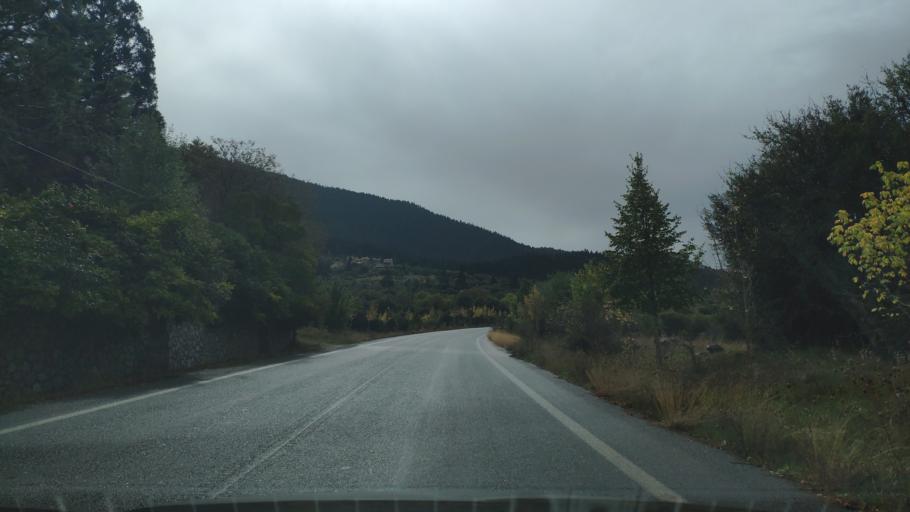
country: GR
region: Peloponnese
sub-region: Nomos Arkadias
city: Langadhia
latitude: 37.6703
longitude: 22.1941
